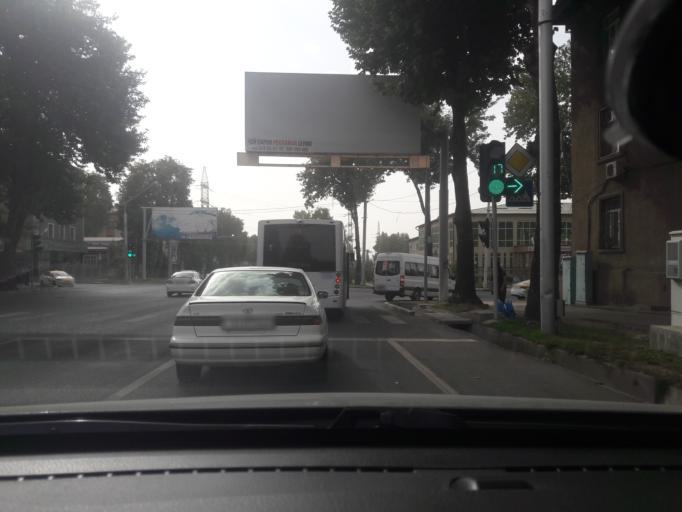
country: TJ
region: Dushanbe
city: Dushanbe
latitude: 38.5757
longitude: 68.8045
